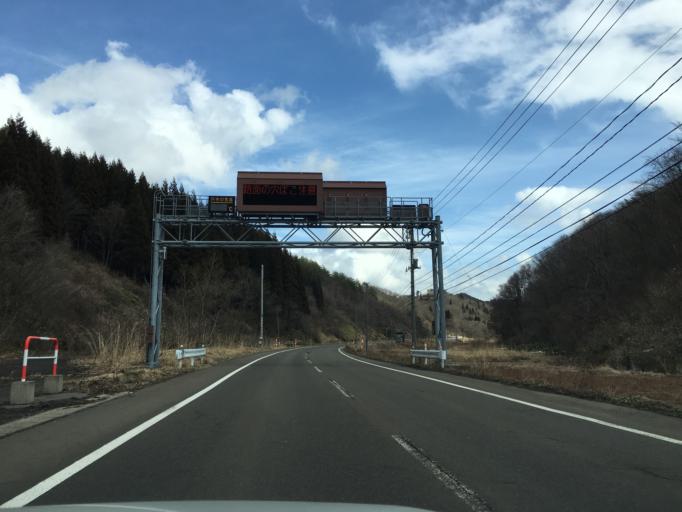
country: JP
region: Akita
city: Odate
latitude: 40.1862
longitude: 140.5047
